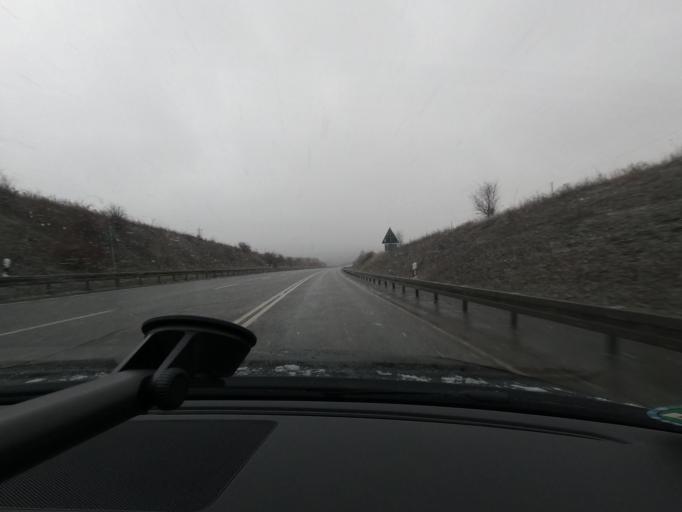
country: DE
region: Thuringia
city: Dingelstadt
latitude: 51.3243
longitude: 10.3288
